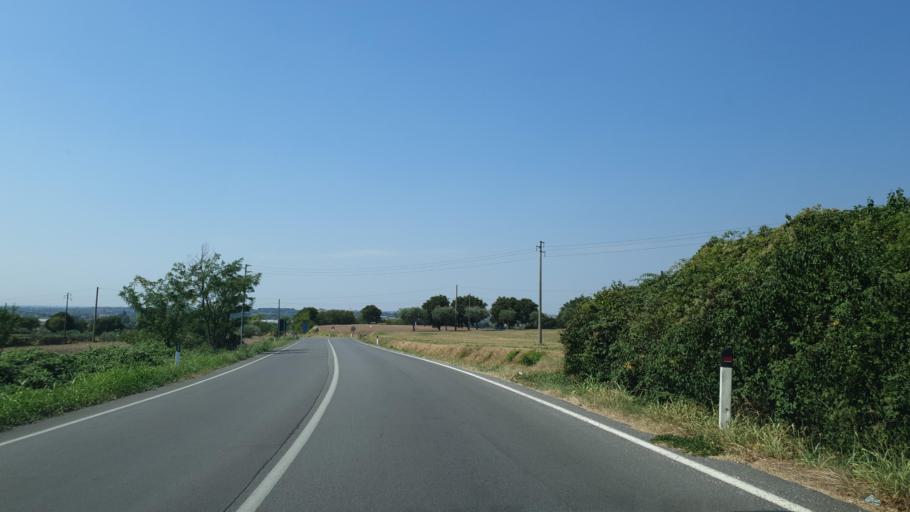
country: IT
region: Lombardy
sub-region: Provincia di Brescia
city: Lonato
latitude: 45.4747
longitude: 10.4759
